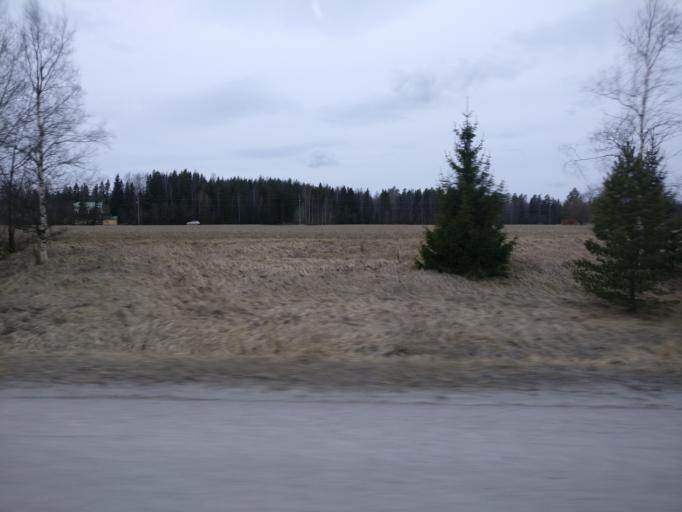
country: FI
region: Uusimaa
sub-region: Helsinki
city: Kilo
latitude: 60.3314
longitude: 24.8212
